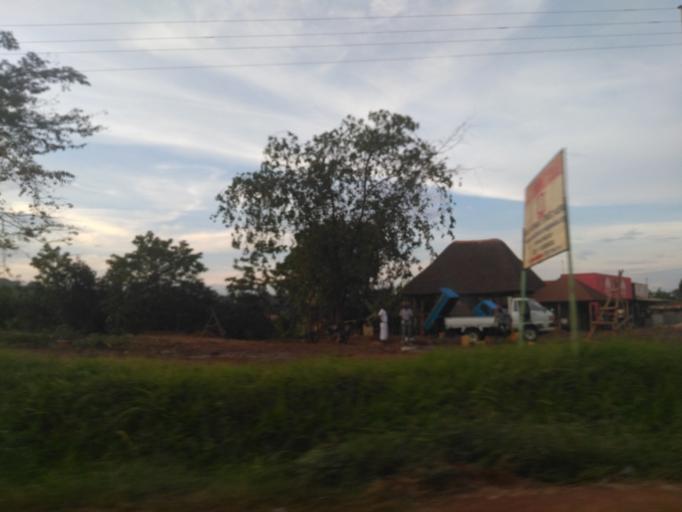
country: UG
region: Central Region
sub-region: Buikwe District
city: Njeru
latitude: 0.4387
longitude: 33.1749
